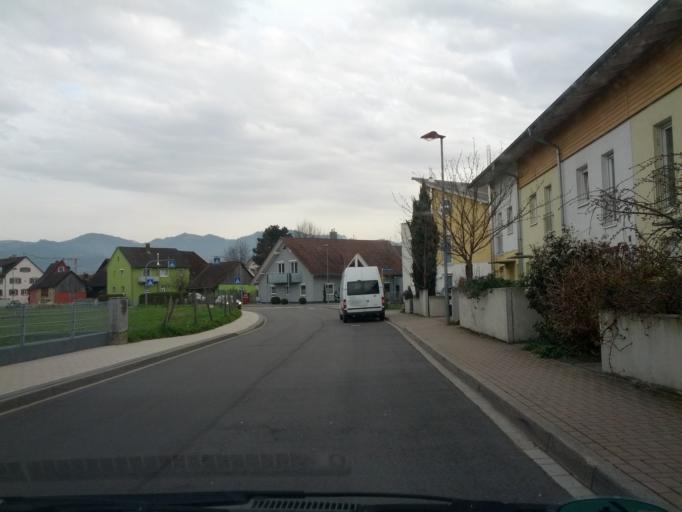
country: DE
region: Baden-Wuerttemberg
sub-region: Freiburg Region
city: Pfaffenweiler
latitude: 47.9203
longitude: 7.7392
